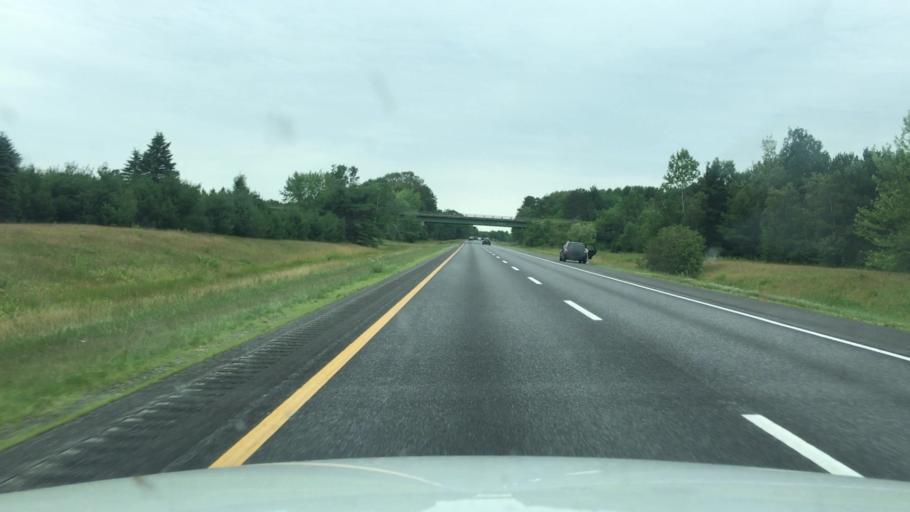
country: US
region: Maine
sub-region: Sagadahoc County
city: Richmond
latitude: 44.1306
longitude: -69.8471
